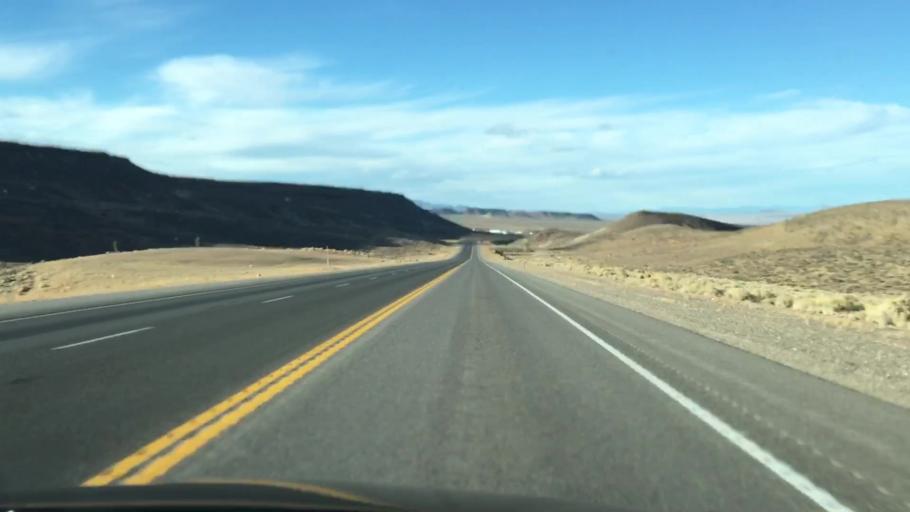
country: US
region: Nevada
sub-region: Esmeralda County
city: Goldfield
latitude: 37.6841
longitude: -117.2309
